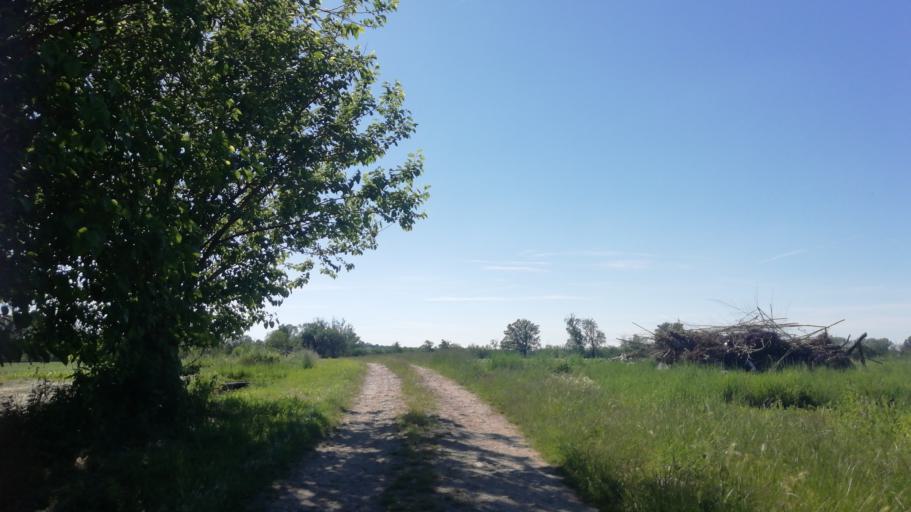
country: IT
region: Emilia-Romagna
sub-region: Provincia di Piacenza
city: Borgonovo Valtidone
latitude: 44.9932
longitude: 9.4662
